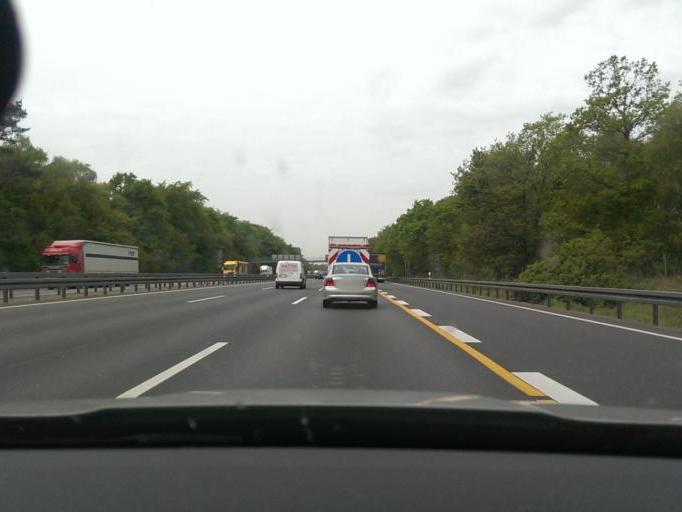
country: DE
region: Lower Saxony
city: Lehrte
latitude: 52.3953
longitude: 9.9178
